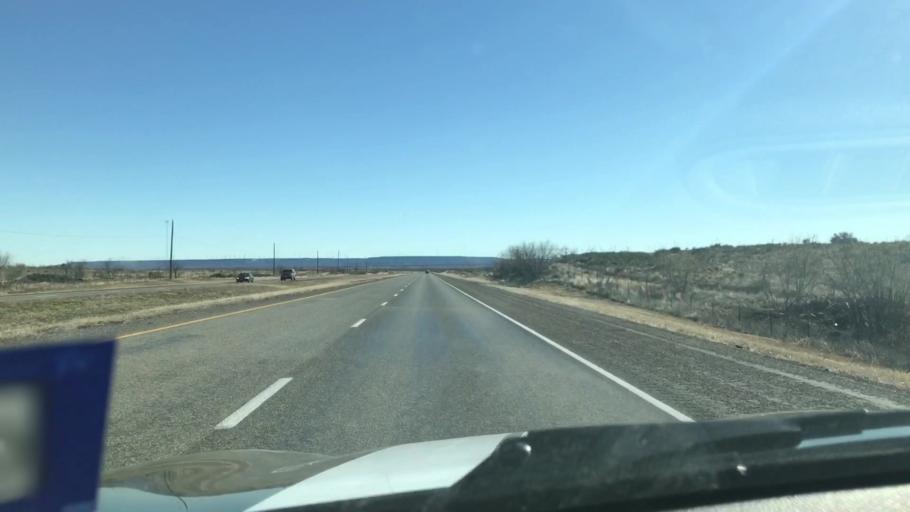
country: US
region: Texas
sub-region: Garza County
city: Post
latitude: 33.0812
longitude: -101.2413
